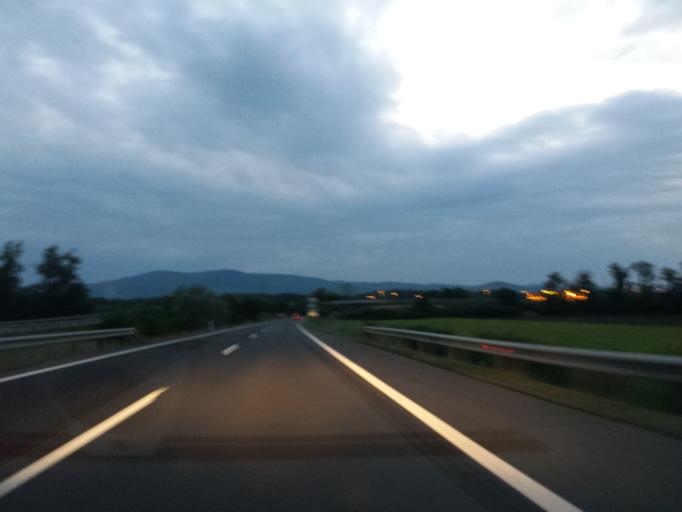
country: AT
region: Lower Austria
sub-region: Politischer Bezirk Modling
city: Guntramsdorf
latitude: 48.0279
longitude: 16.3416
